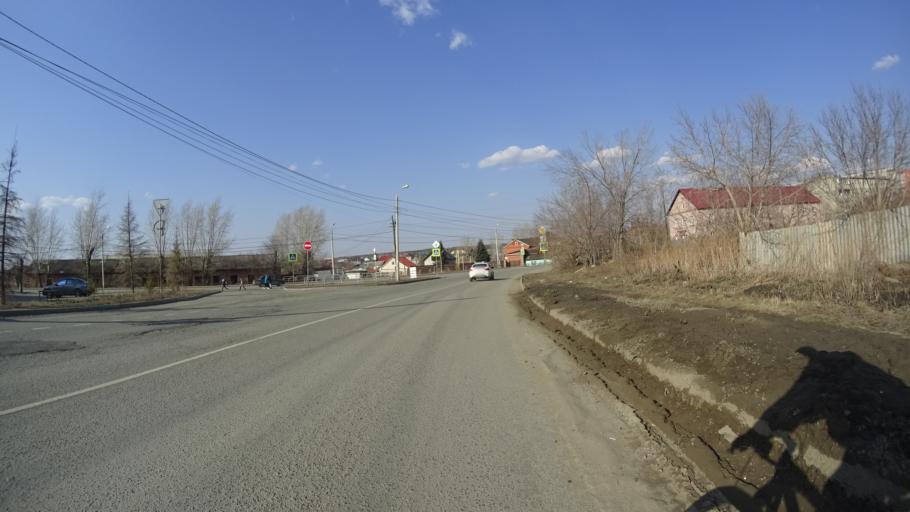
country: RU
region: Chelyabinsk
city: Novosineglazovskiy
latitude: 55.1111
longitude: 61.3324
